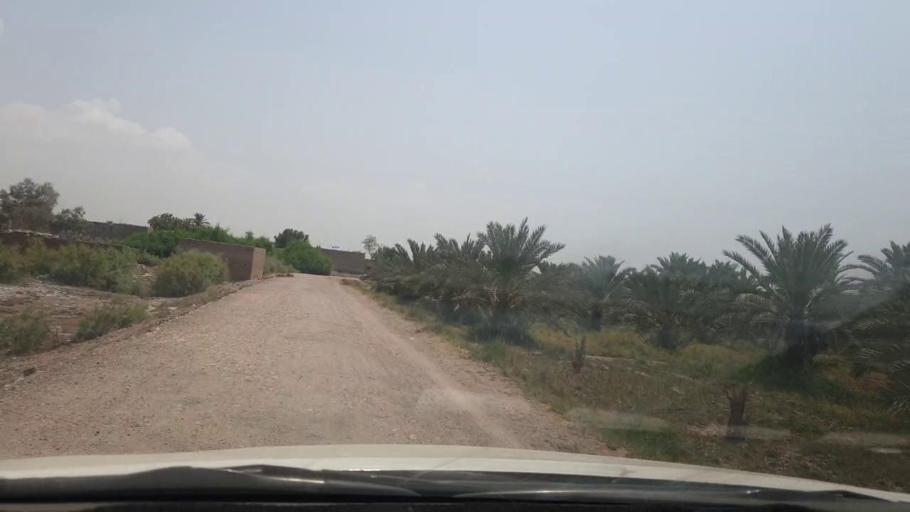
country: PK
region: Sindh
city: Khairpur
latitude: 27.5596
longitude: 68.8293
